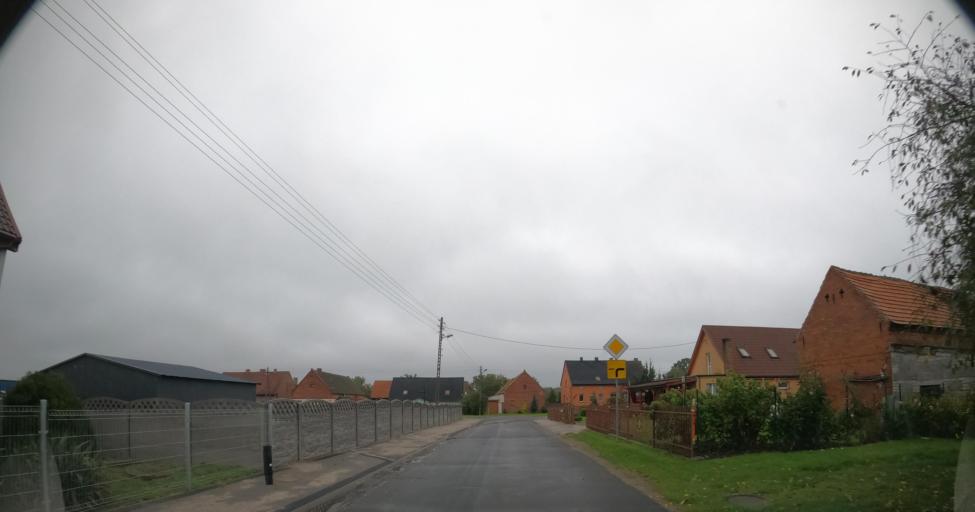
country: PL
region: West Pomeranian Voivodeship
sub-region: Powiat pyrzycki
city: Kozielice
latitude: 53.0744
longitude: 14.7873
